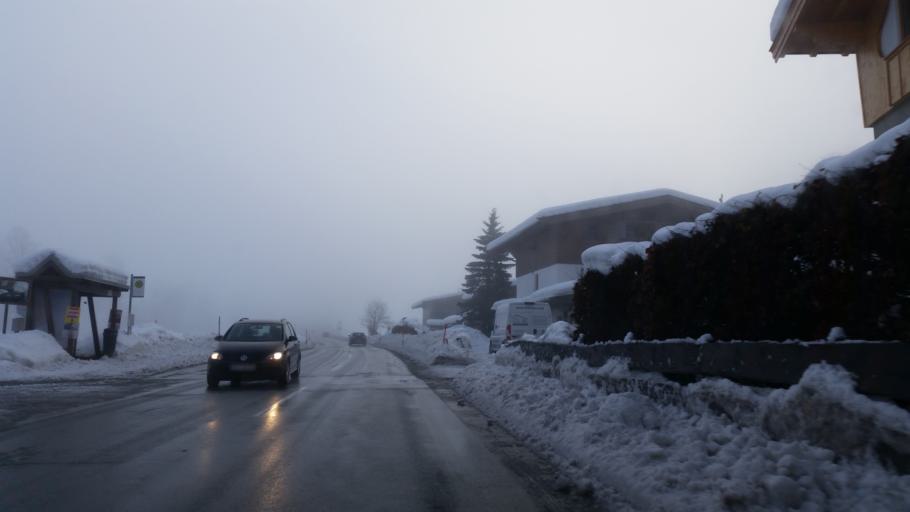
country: AT
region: Tyrol
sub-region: Politischer Bezirk Kitzbuhel
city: Sankt Johann in Tirol
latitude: 47.5083
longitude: 12.4663
